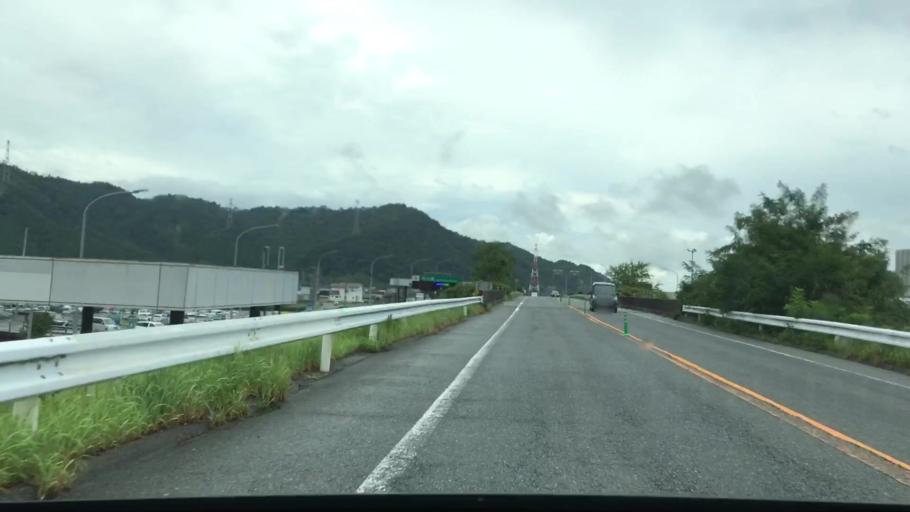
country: JP
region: Hyogo
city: Himeji
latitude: 34.9848
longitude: 134.7700
